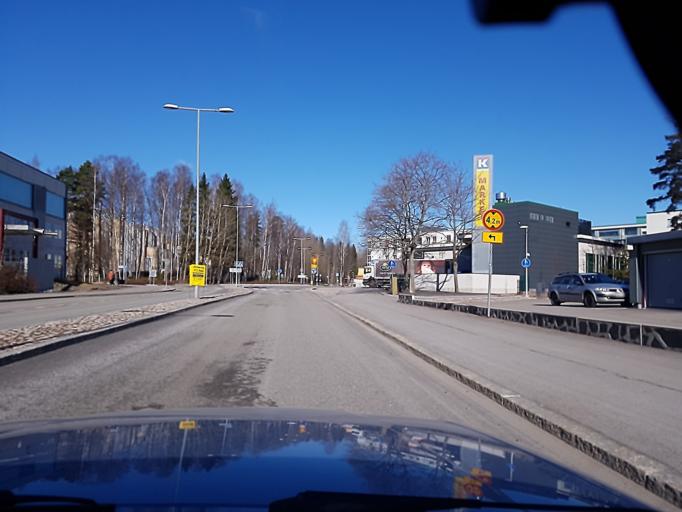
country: FI
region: Uusimaa
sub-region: Helsinki
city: Teekkarikylae
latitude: 60.2702
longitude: 24.8567
